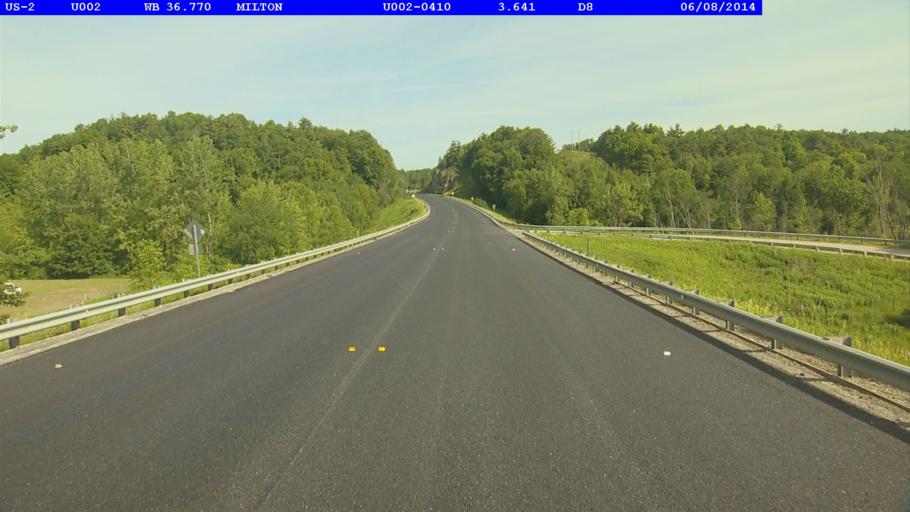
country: US
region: Vermont
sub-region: Chittenden County
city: Colchester
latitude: 44.6042
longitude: -73.2049
